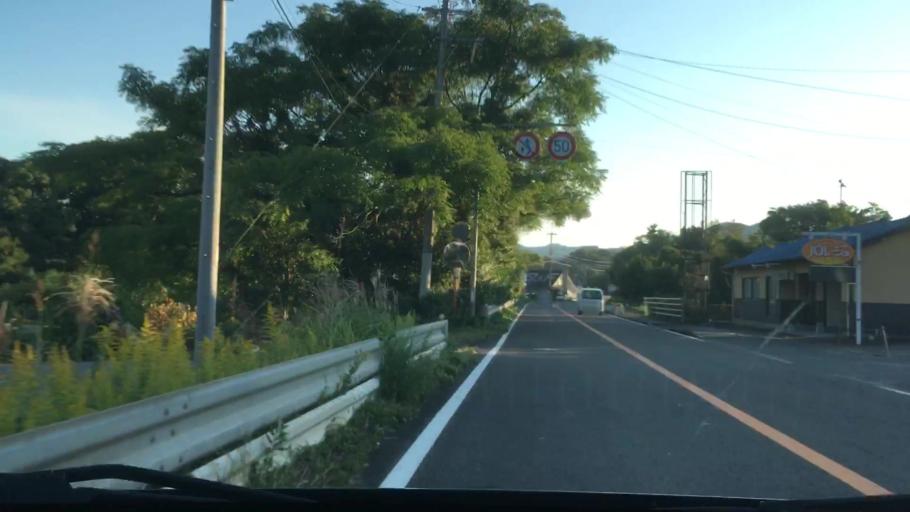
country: JP
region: Nagasaki
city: Sasebo
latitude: 33.0194
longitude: 129.7364
